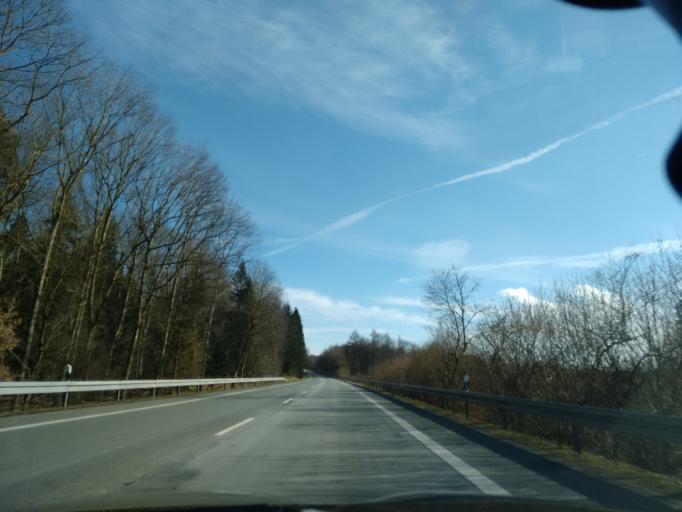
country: DE
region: North Rhine-Westphalia
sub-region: Regierungsbezirk Detmold
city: Altenbeken
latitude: 51.6961
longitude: 8.9566
